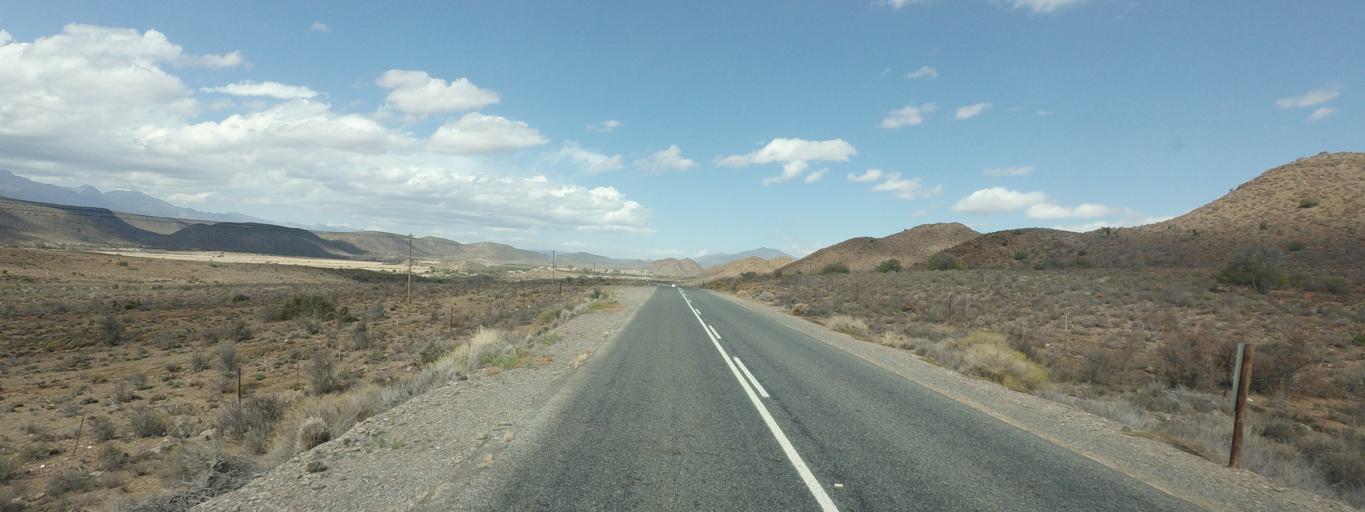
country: ZA
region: Western Cape
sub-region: Eden District Municipality
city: Ladismith
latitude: -33.5994
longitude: 21.1238
